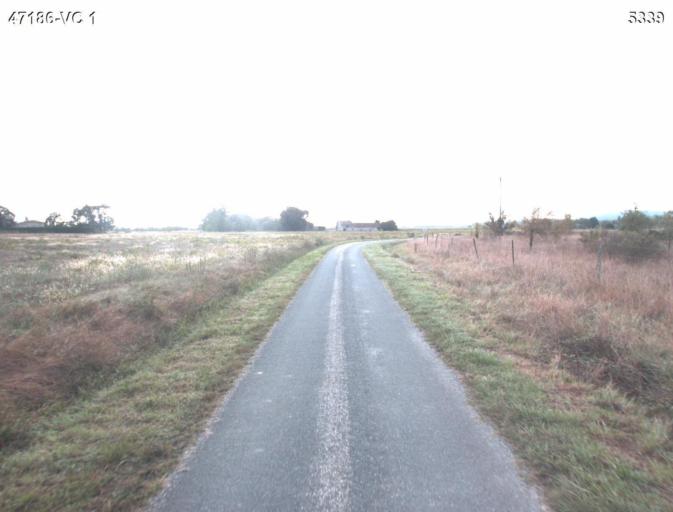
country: FR
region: Aquitaine
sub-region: Departement du Lot-et-Garonne
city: Port-Sainte-Marie
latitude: 44.2305
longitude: 0.4333
